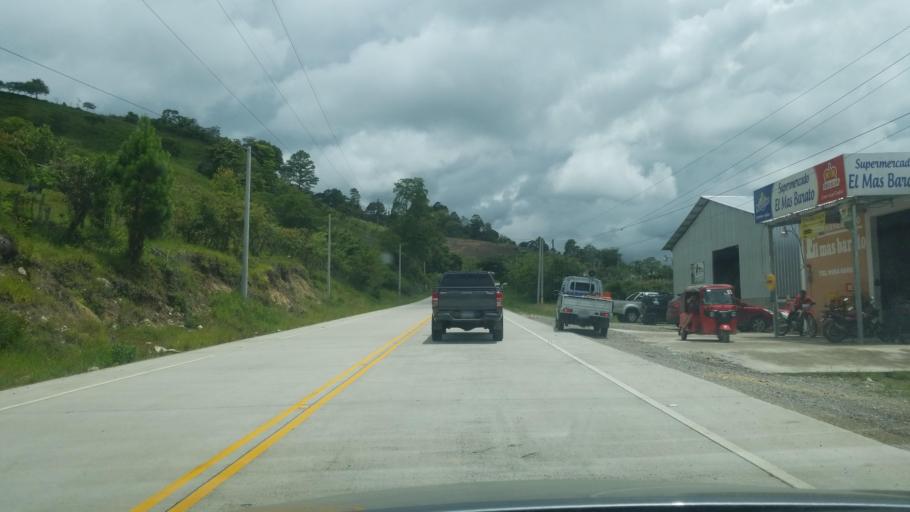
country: HN
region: Copan
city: San Jeronimo
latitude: 14.9851
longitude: -88.8595
